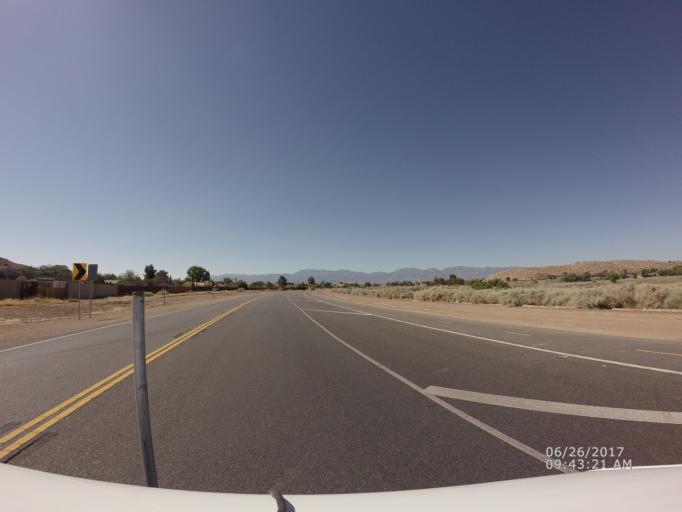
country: US
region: California
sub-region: Los Angeles County
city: Lake Los Angeles
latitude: 34.6054
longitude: -117.8243
